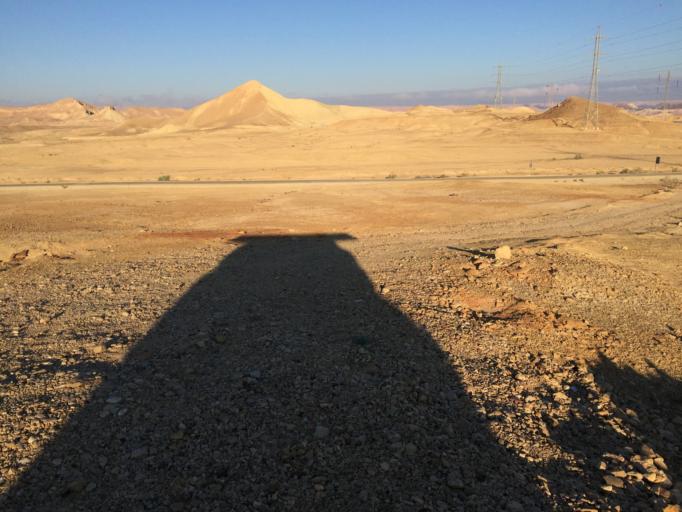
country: IL
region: Southern District
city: Mitzpe Ramon
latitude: 30.5285
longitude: 34.9205
